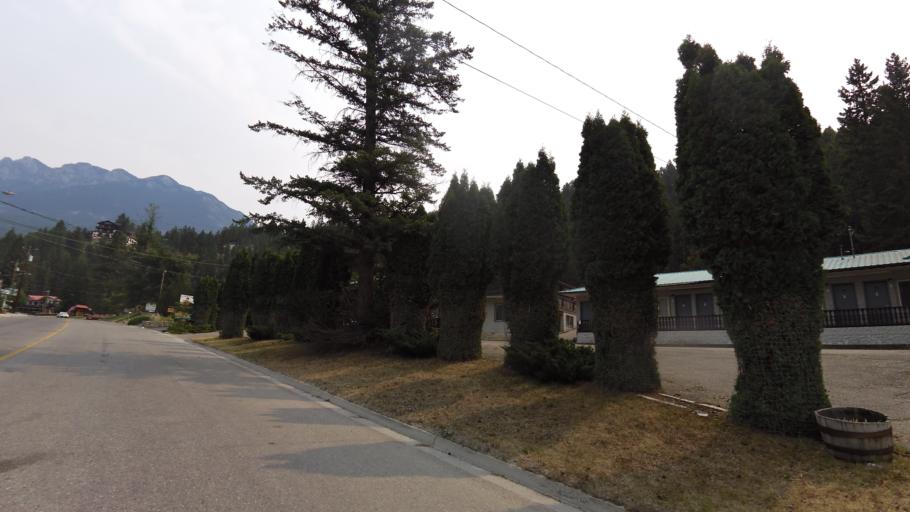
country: CA
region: British Columbia
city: Invermere
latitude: 50.6253
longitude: -116.0676
